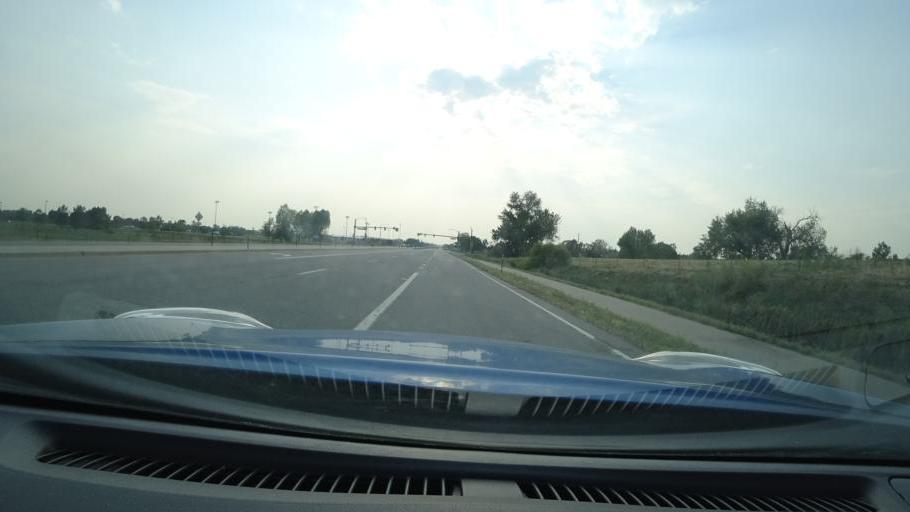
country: US
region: Colorado
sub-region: Adams County
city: Aurora
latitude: 39.7403
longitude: -104.7614
